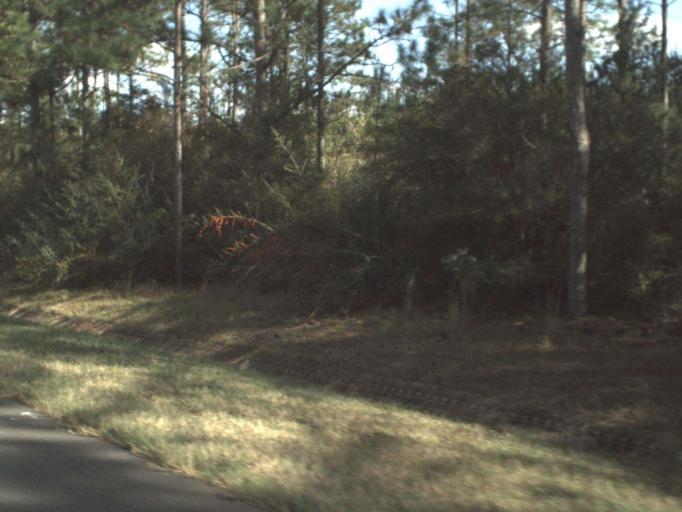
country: US
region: Florida
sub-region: Holmes County
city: Bonifay
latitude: 30.7882
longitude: -85.7587
